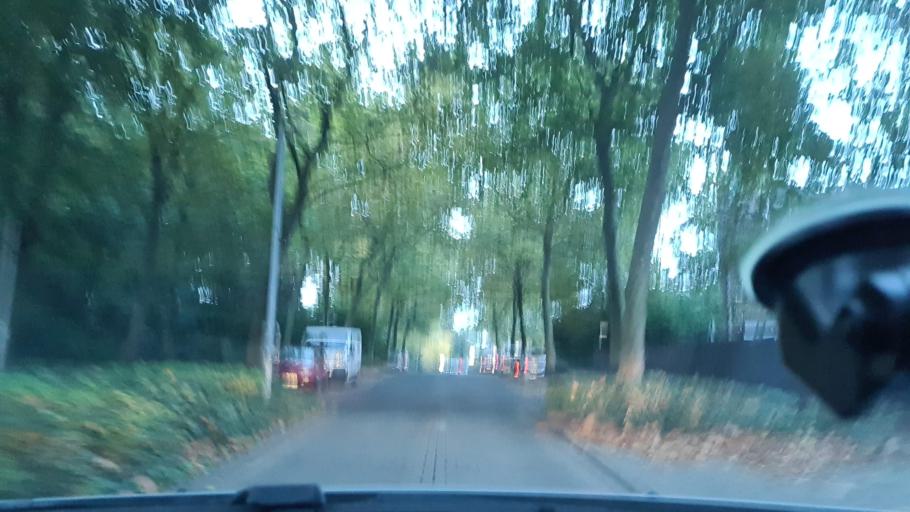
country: DE
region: North Rhine-Westphalia
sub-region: Regierungsbezirk Dusseldorf
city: Viersen
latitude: 51.2792
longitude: 6.3672
